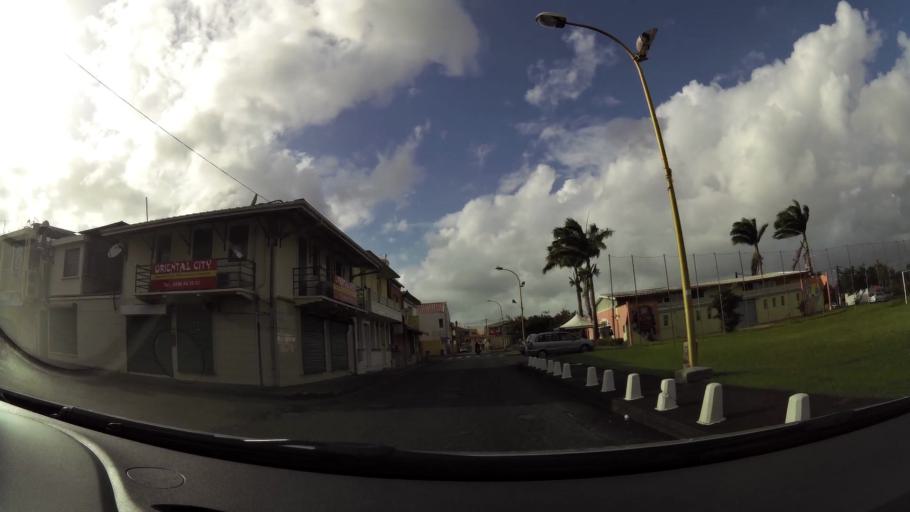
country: MQ
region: Martinique
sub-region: Martinique
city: Ducos
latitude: 14.5289
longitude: -60.9801
